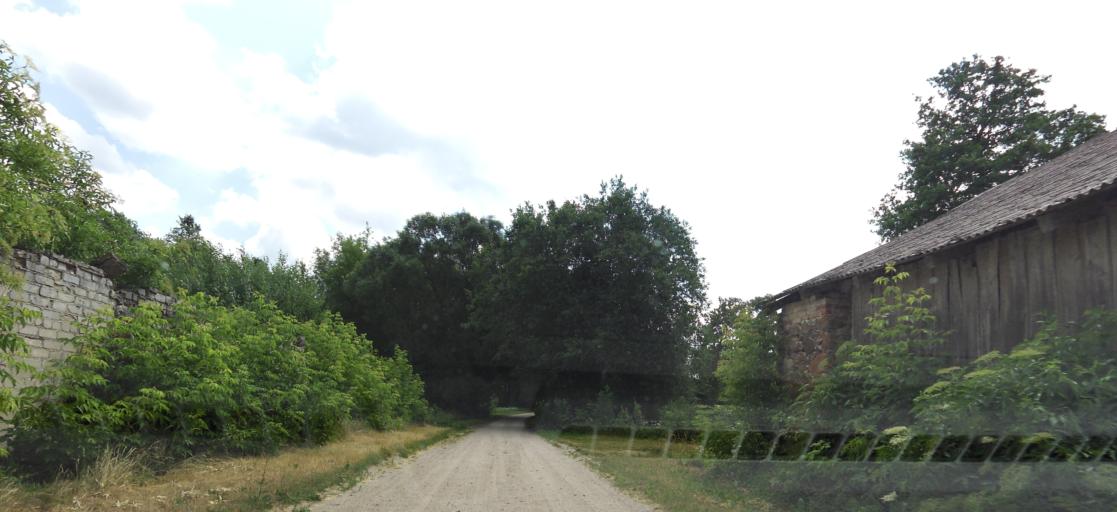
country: LT
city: Obeliai
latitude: 56.1125
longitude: 25.0045
